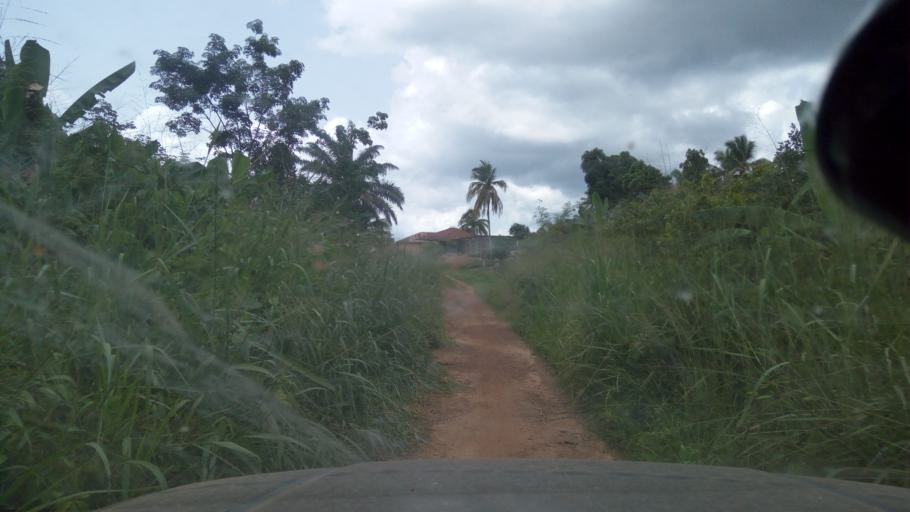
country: SL
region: Eastern Province
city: Segbwema
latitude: 7.9826
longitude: -11.0097
